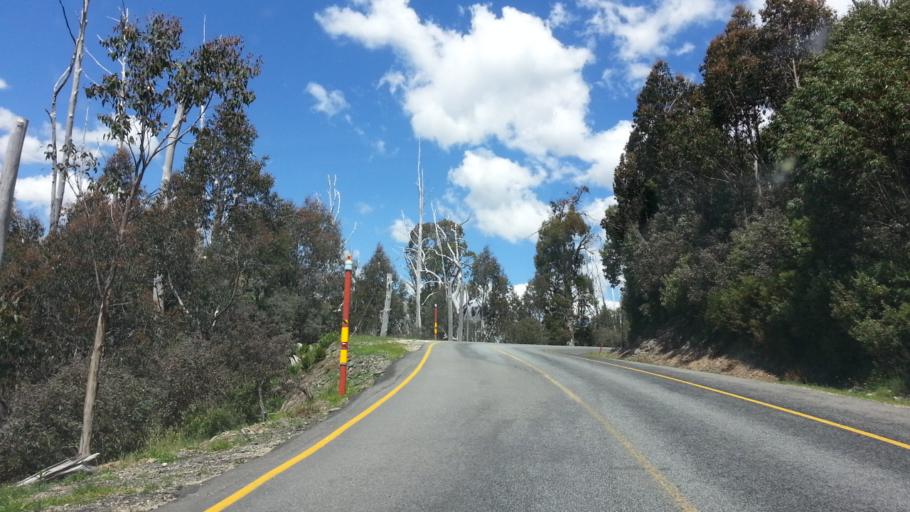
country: AU
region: Victoria
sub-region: Alpine
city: Mount Beauty
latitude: -36.8511
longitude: 147.2707
